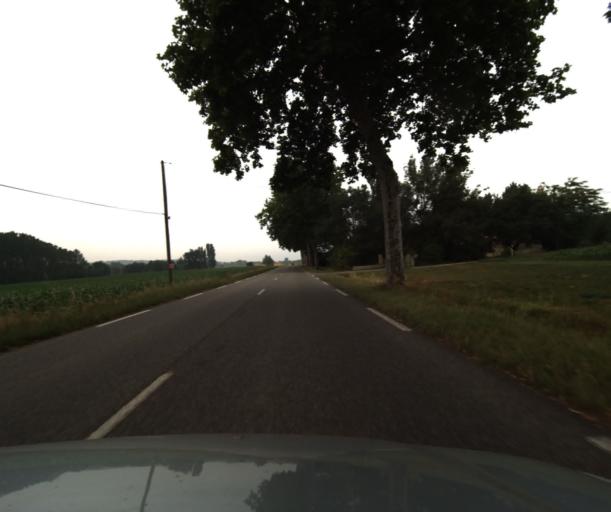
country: FR
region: Midi-Pyrenees
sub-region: Departement du Tarn-et-Garonne
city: Beaumont-de-Lomagne
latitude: 43.8346
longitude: 0.9241
